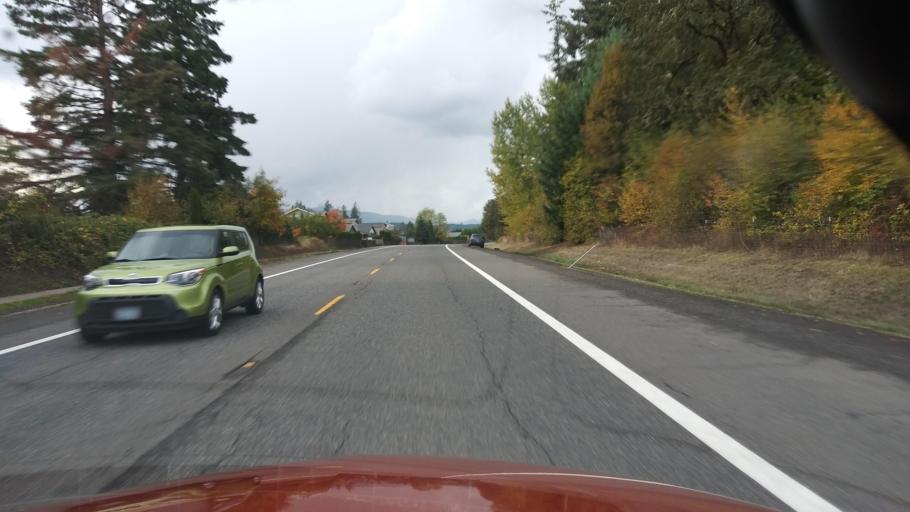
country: US
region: Oregon
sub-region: Washington County
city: Forest Grove
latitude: 45.5301
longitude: -123.0946
